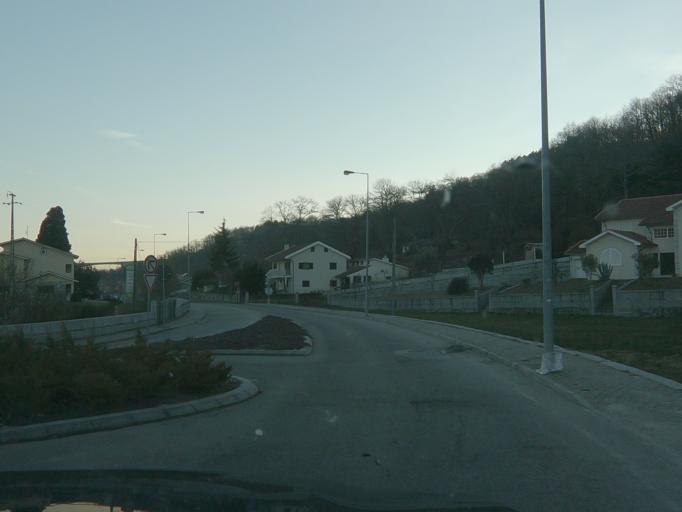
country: PT
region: Vila Real
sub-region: Vila Pouca de Aguiar
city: Vila Pouca de Aguiar
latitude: 41.4979
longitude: -7.6486
